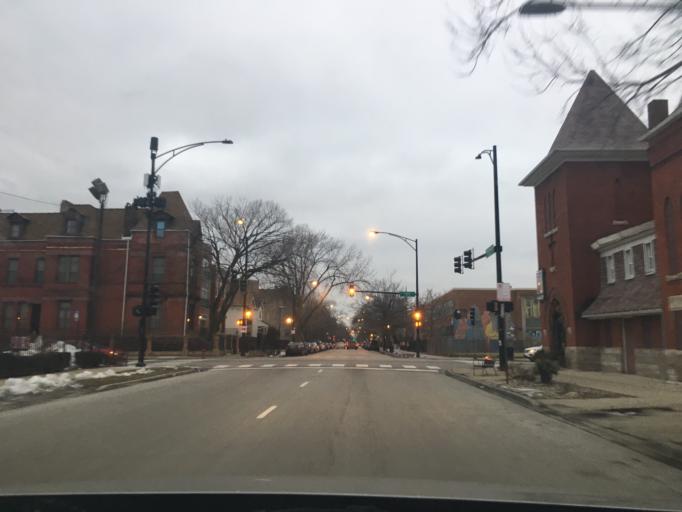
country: US
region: Illinois
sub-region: Cook County
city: Chicago
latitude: 41.8832
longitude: -87.6762
